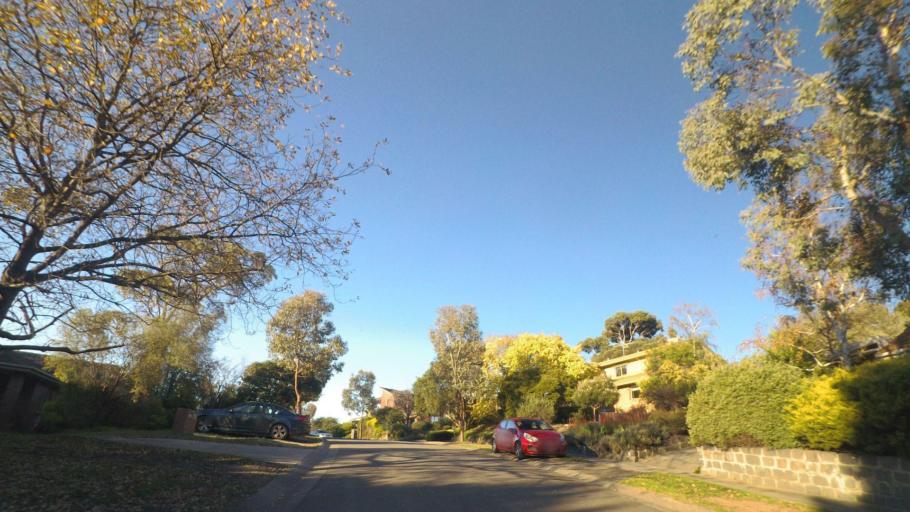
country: AU
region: Victoria
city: Plenty
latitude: -37.6854
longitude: 145.1100
